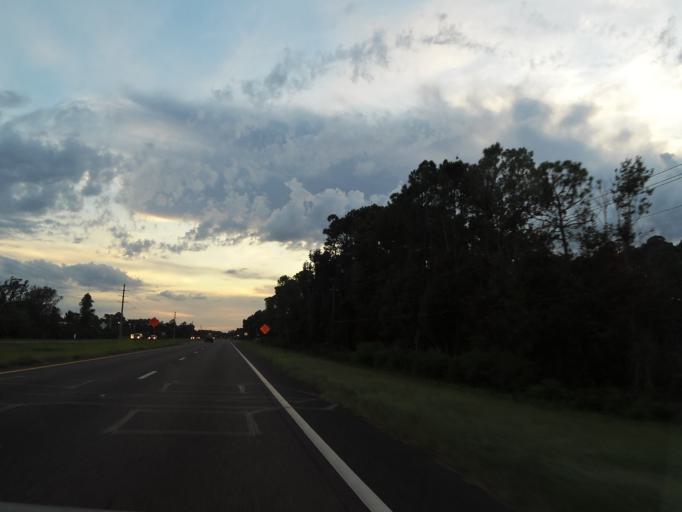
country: US
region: Florida
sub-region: Nassau County
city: Fernandina Beach
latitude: 30.6226
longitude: -81.4953
